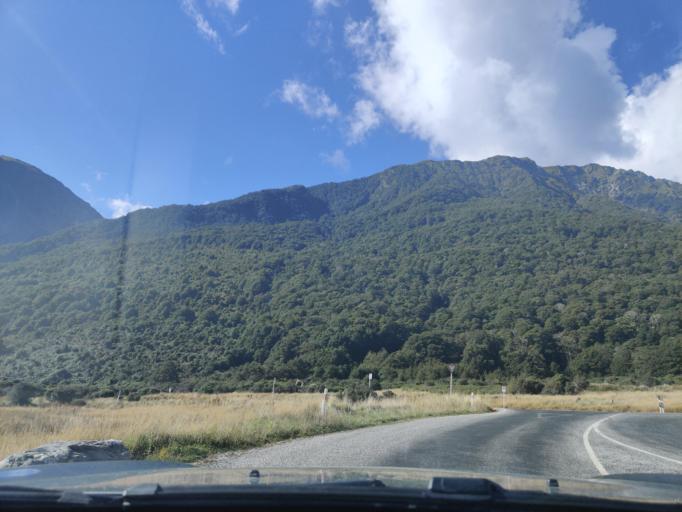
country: NZ
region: Otago
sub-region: Queenstown-Lakes District
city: Wanaka
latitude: -44.1604
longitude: 169.2879
